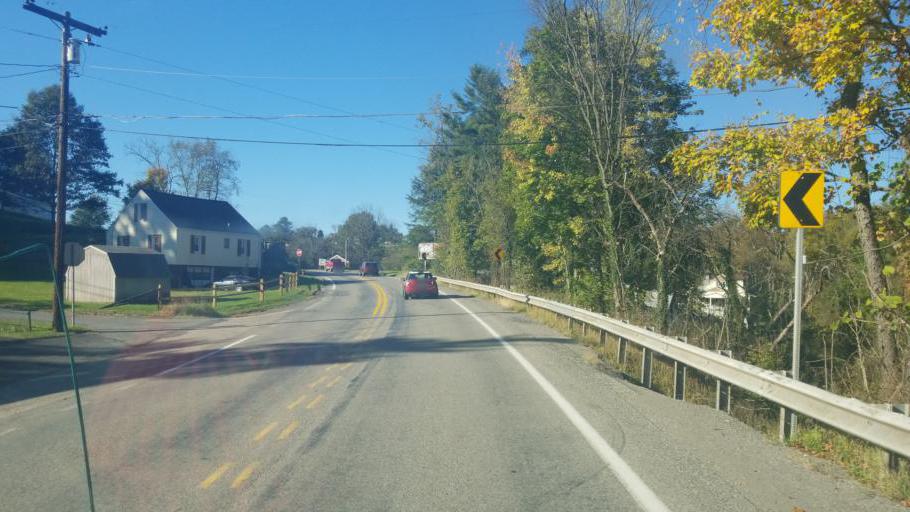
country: US
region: Pennsylvania
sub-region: Allegheny County
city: Imperial
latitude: 40.4480
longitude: -80.2448
